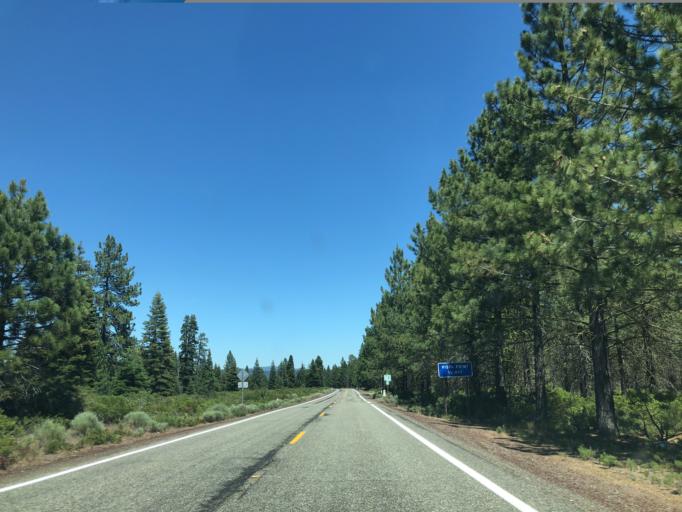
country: US
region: California
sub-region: Shasta County
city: Burney
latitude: 40.6198
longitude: -121.4877
